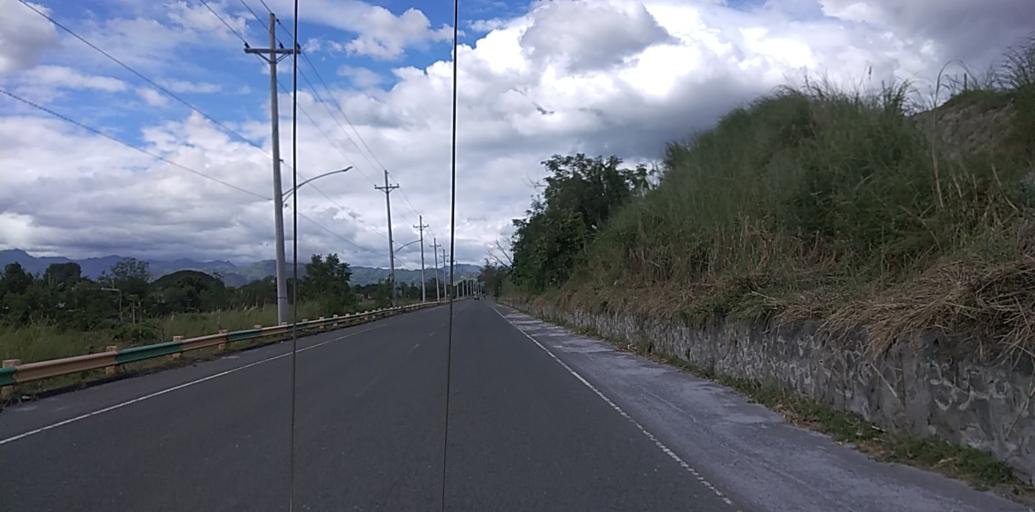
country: PH
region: Central Luzon
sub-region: Province of Pampanga
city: Dolores
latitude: 15.0950
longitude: 120.5303
